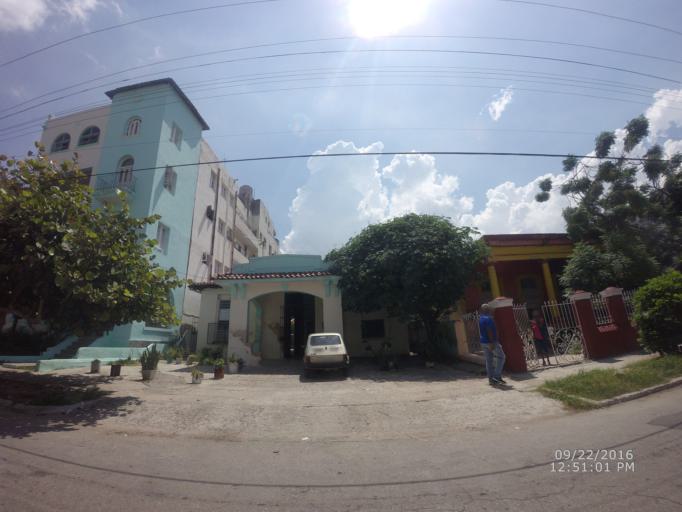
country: CU
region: La Habana
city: Havana
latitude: 23.1399
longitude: -82.3979
